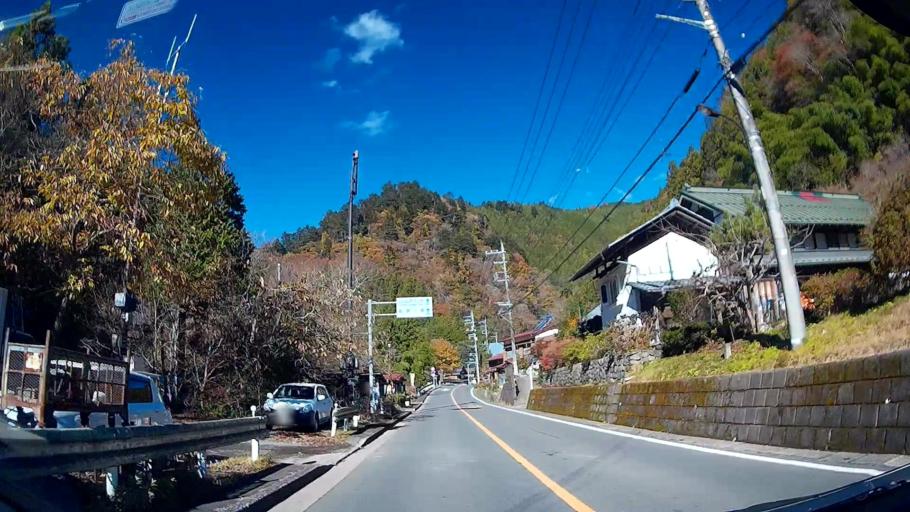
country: JP
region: Yamanashi
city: Uenohara
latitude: 35.7022
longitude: 139.1329
